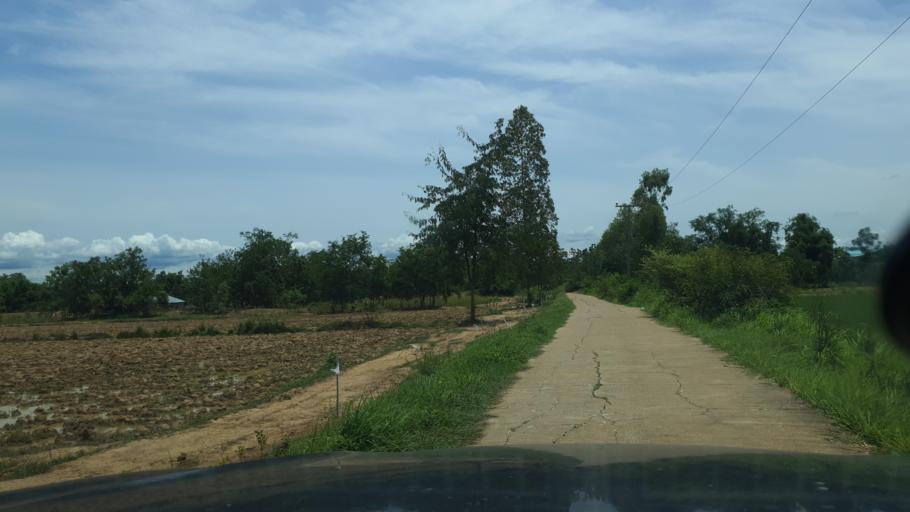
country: TH
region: Sukhothai
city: Ban Na
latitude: 17.0910
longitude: 99.6871
